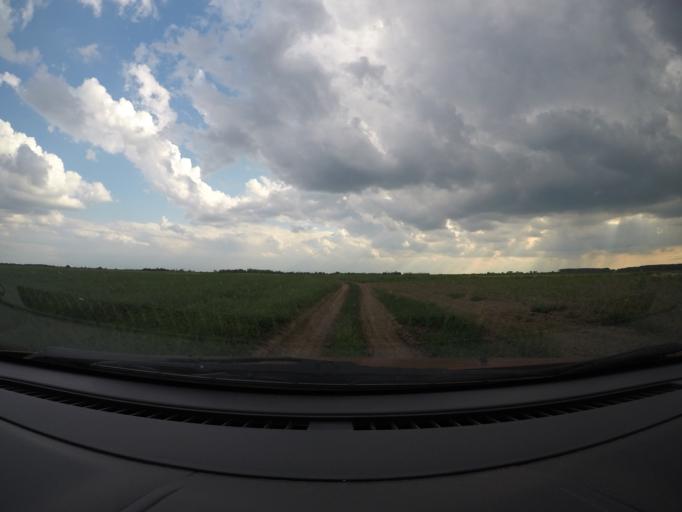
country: RS
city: Uzdin
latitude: 45.2052
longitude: 20.6017
